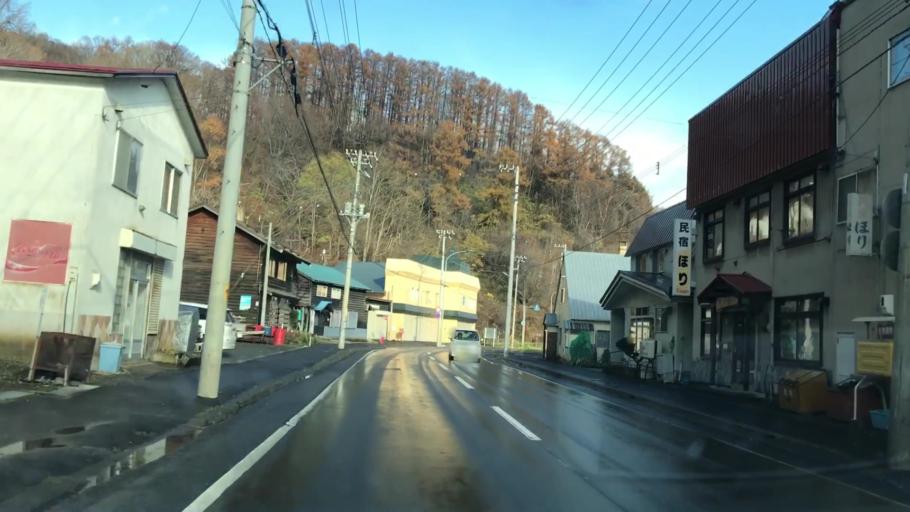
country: JP
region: Hokkaido
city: Yoichi
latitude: 43.2738
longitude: 140.6355
